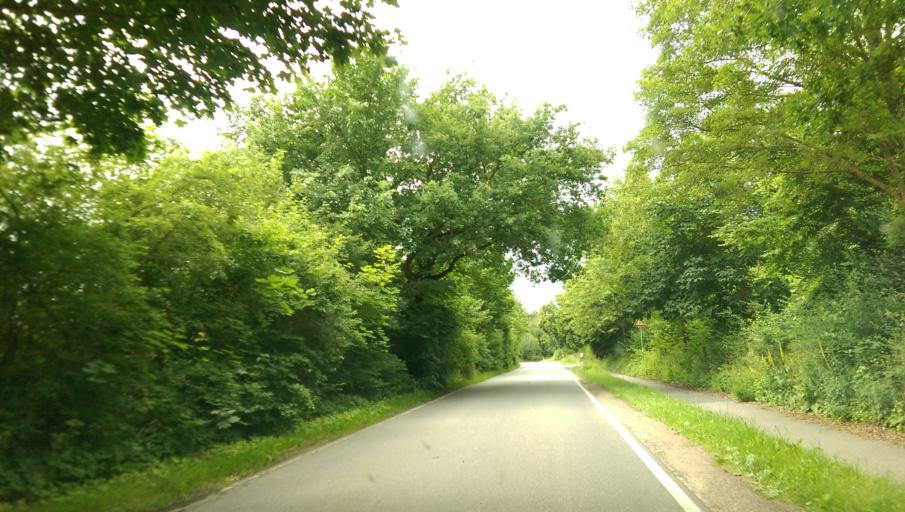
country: DE
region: Schleswig-Holstein
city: Ratekau
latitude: 53.9879
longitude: 10.6948
